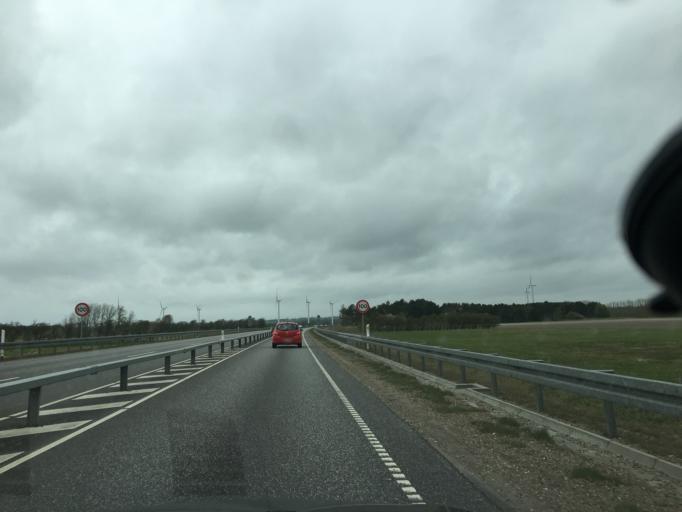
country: DK
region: Zealand
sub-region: Odsherred Kommune
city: Asnaes
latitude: 55.7497
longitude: 11.5844
